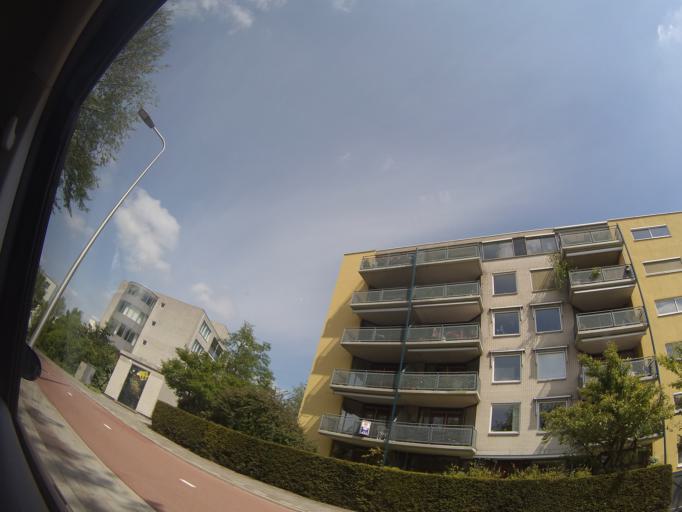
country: NL
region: Utrecht
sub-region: Gemeente Utrecht
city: Utrecht
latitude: 52.1066
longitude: 5.1440
